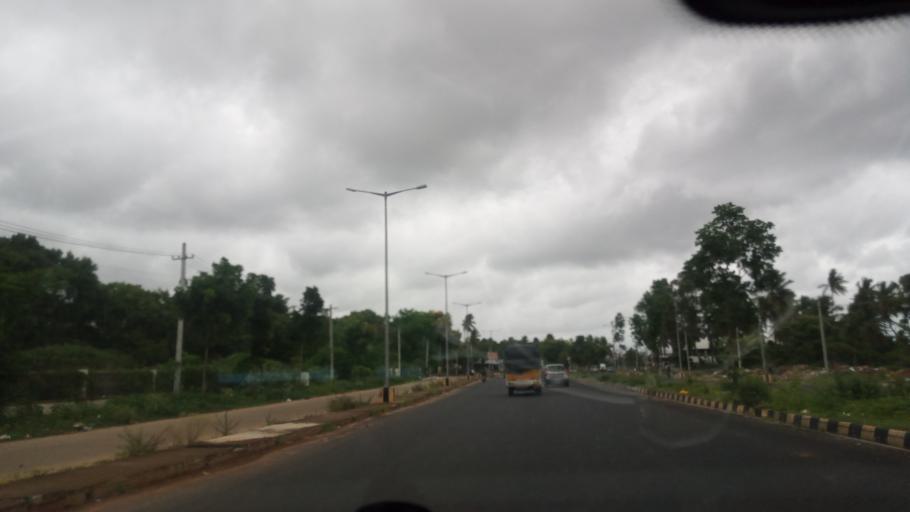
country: IN
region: Karnataka
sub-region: Mysore
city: Mysore
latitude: 12.2997
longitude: 76.6028
